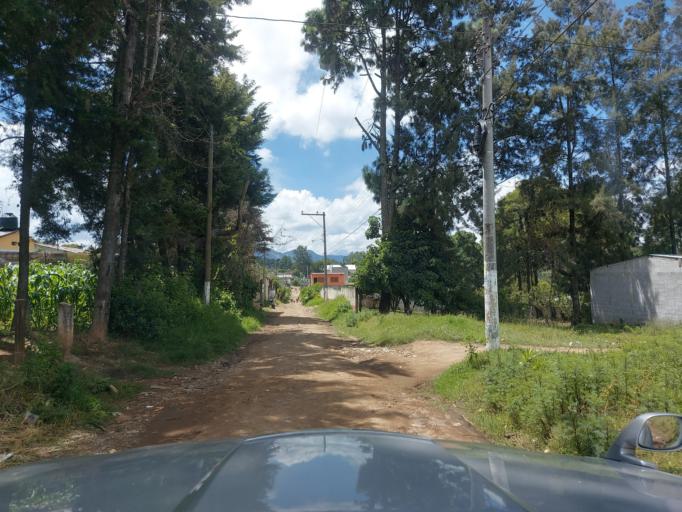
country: GT
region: Chimaltenango
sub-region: Municipio de Chimaltenango
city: Chimaltenango
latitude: 14.6452
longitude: -90.8143
